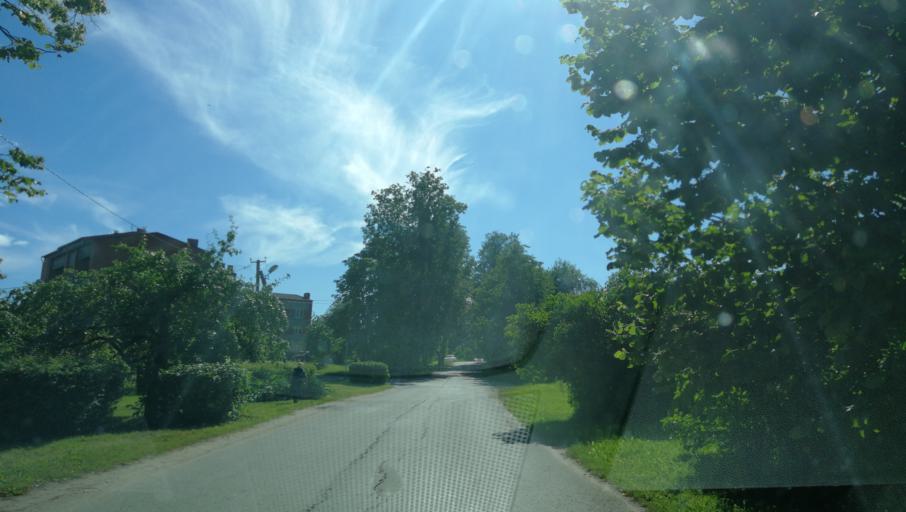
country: LV
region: Cesvaine
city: Cesvaine
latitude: 56.9680
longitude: 26.3033
